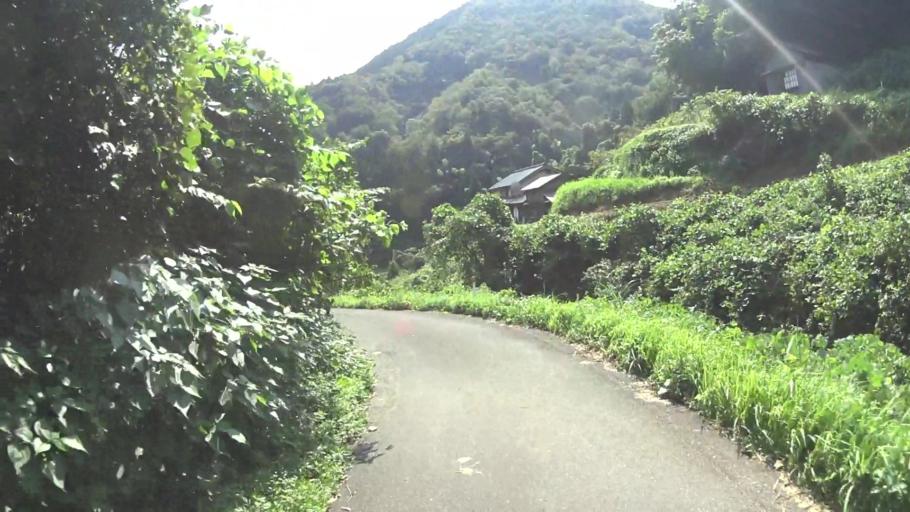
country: JP
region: Kyoto
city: Miyazu
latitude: 35.6574
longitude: 135.2441
